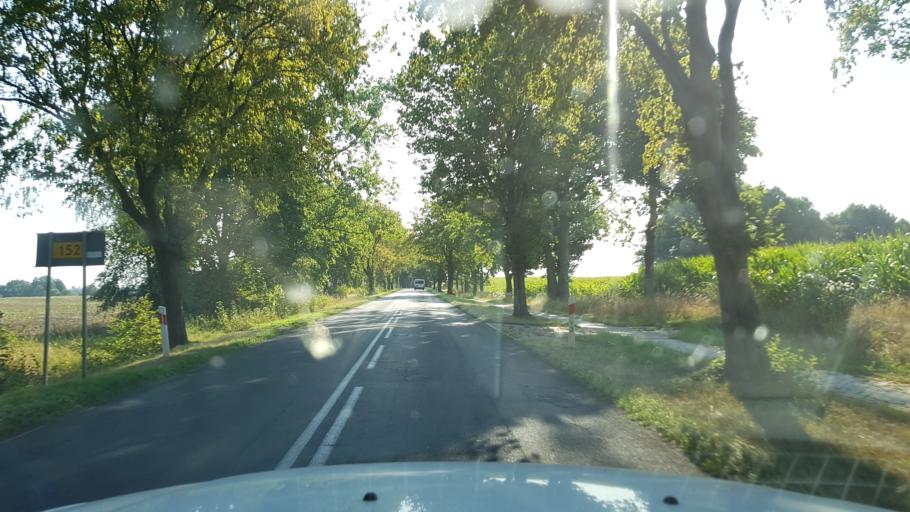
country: PL
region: West Pomeranian Voivodeship
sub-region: Powiat lobeski
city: Resko
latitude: 53.7756
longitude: 15.3784
